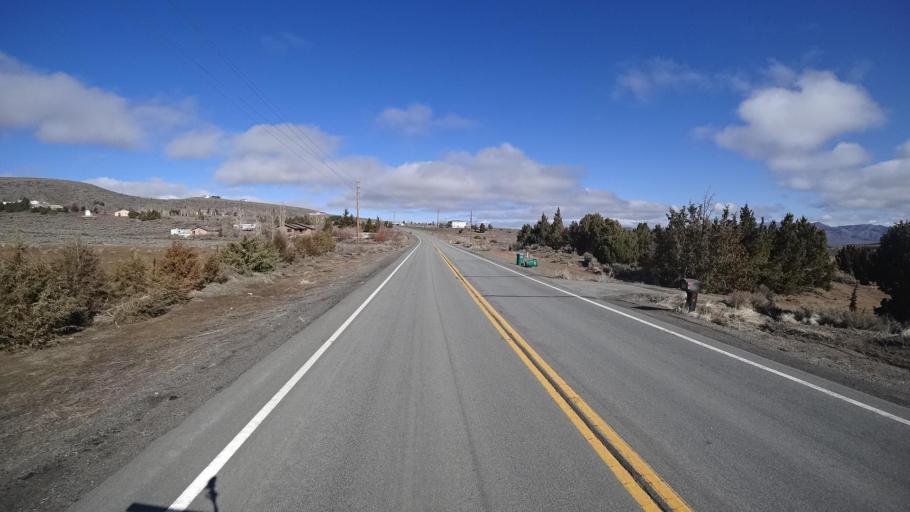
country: US
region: Nevada
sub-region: Washoe County
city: Cold Springs
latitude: 39.7830
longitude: -119.8955
